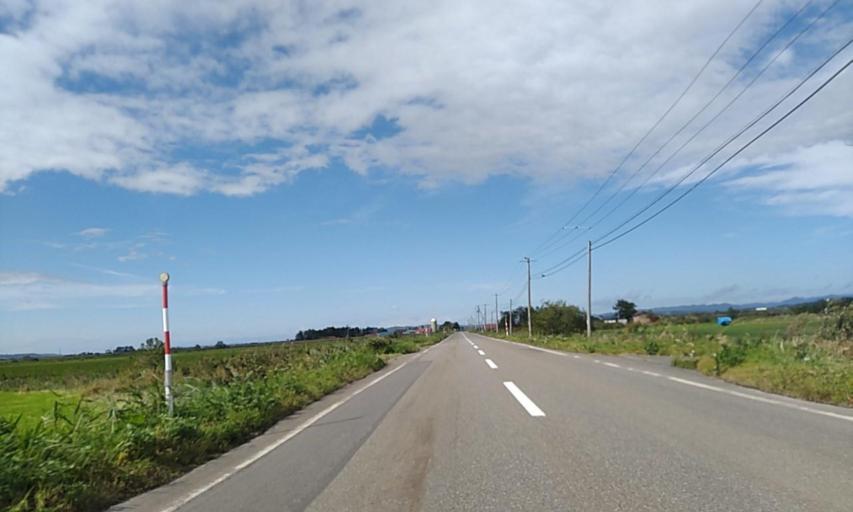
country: JP
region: Hokkaido
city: Obihiro
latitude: 42.7172
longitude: 143.6351
